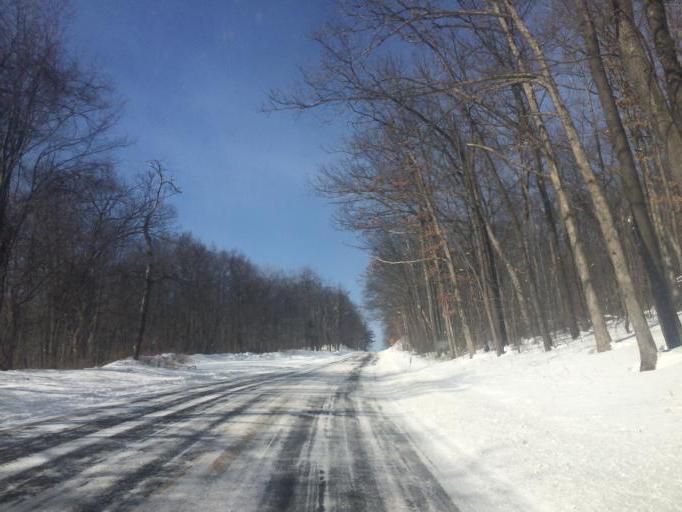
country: US
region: Pennsylvania
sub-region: Centre County
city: Stormstown
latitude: 40.8810
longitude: -78.0171
